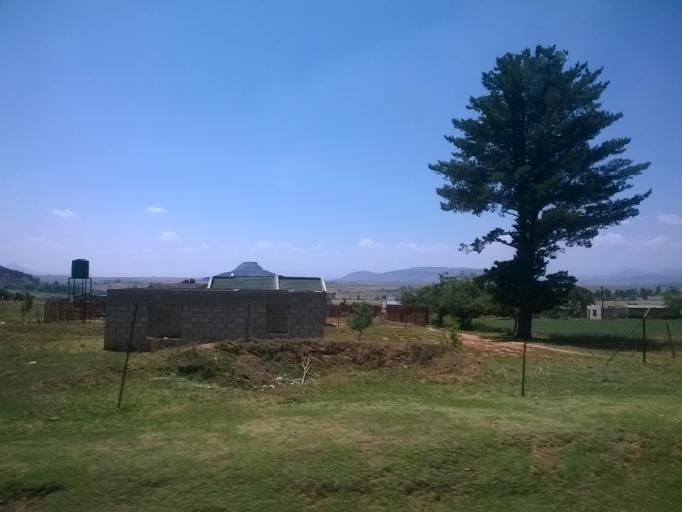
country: LS
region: Leribe
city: Maputsoe
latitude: -28.9612
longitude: 27.9615
